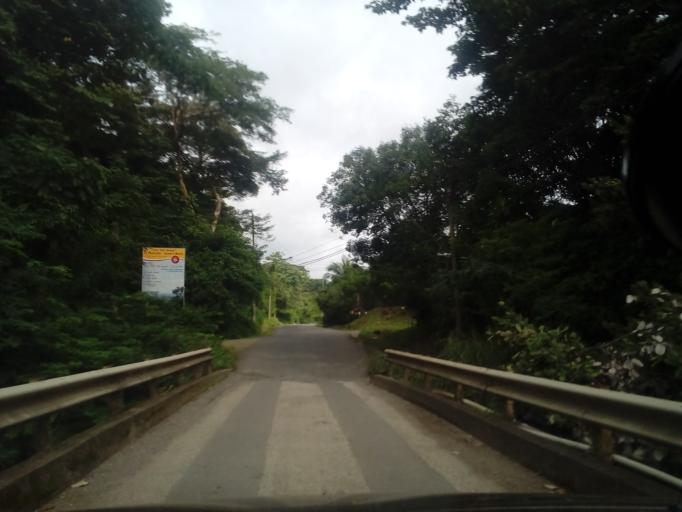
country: CR
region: Guanacaste
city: Samara
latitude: 9.9208
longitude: -85.5345
